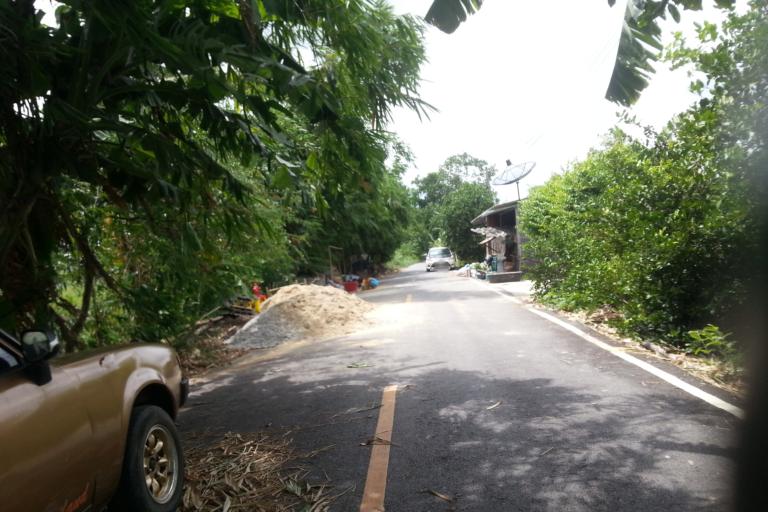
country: TH
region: Pathum Thani
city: Ban Rangsit
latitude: 14.0498
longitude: 100.8240
